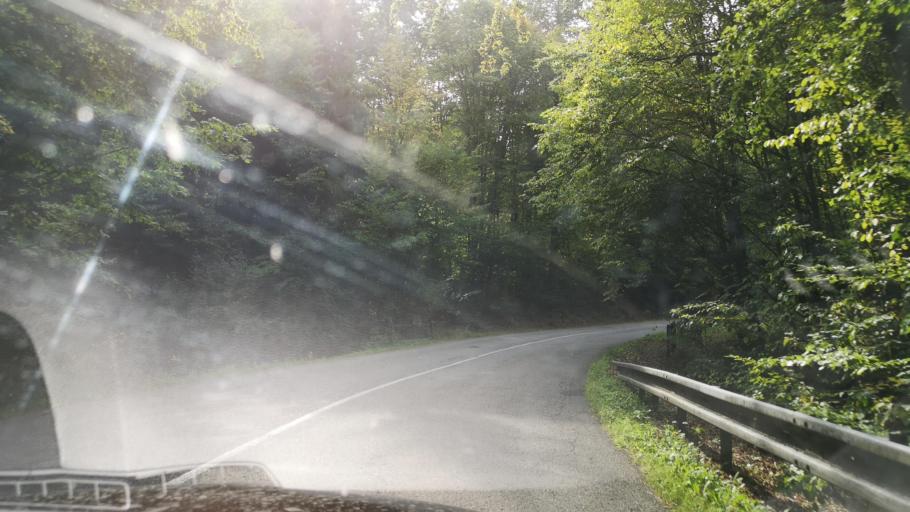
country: SK
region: Banskobystricky
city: Tisovec
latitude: 48.5765
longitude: 19.9772
